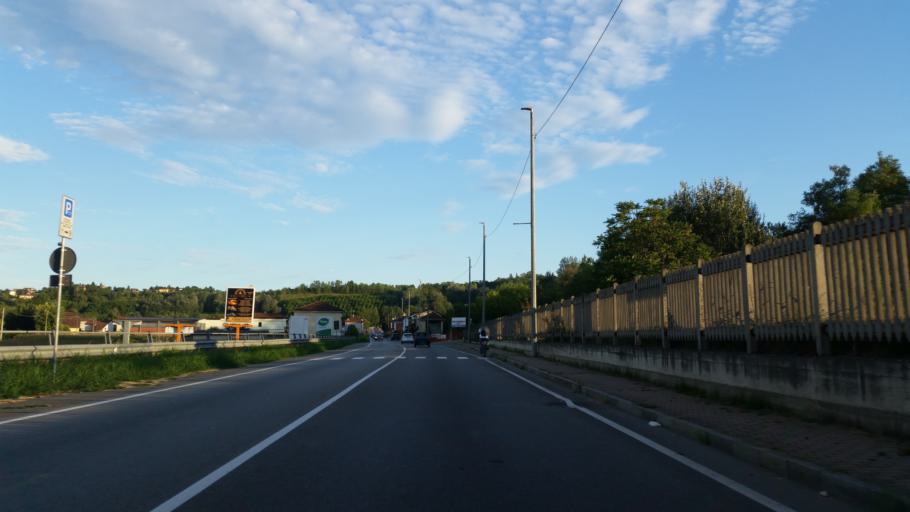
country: IT
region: Piedmont
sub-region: Provincia di Asti
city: Asti
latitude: 44.8830
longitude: 8.2127
